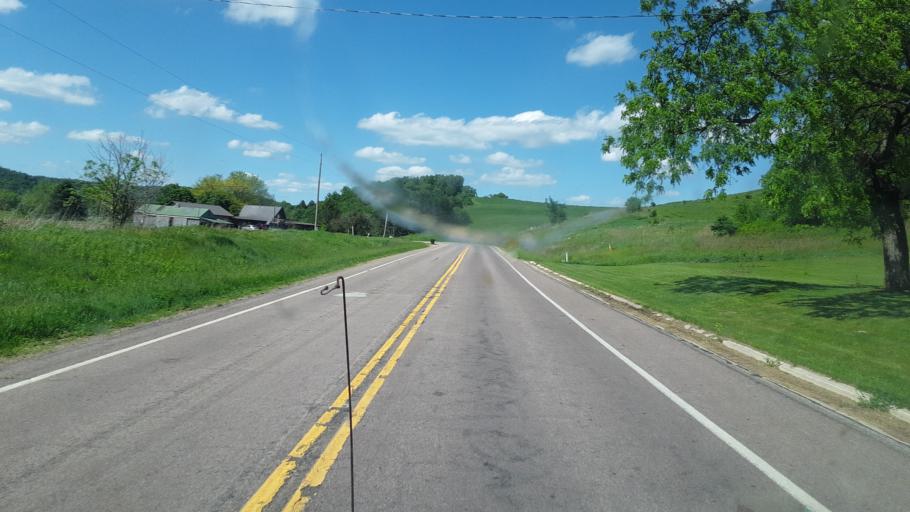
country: US
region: Wisconsin
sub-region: Richland County
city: Richland Center
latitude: 43.3608
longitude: -90.2664
